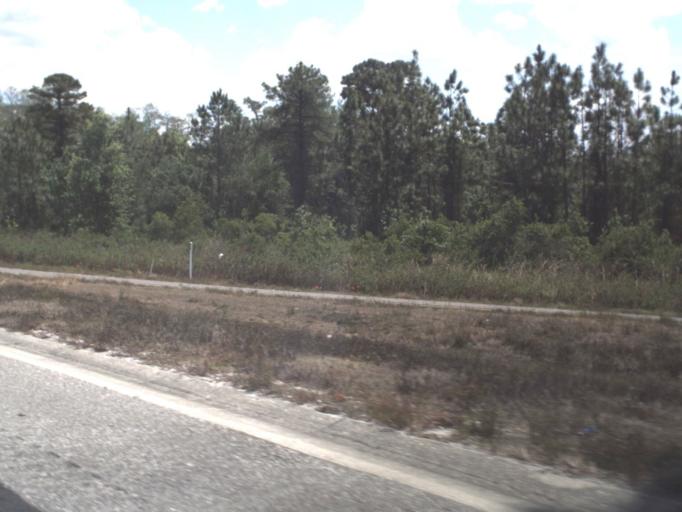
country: US
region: Florida
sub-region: Orange County
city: Wedgefield
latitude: 28.4514
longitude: -81.1573
